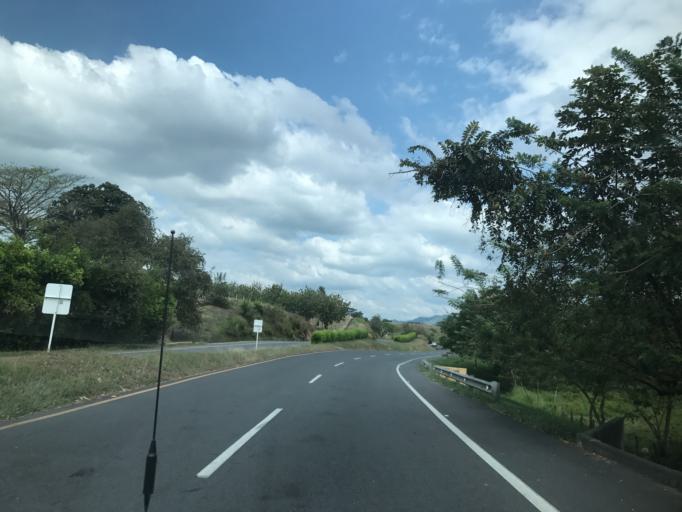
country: CO
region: Valle del Cauca
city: Obando
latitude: 4.6018
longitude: -75.9603
